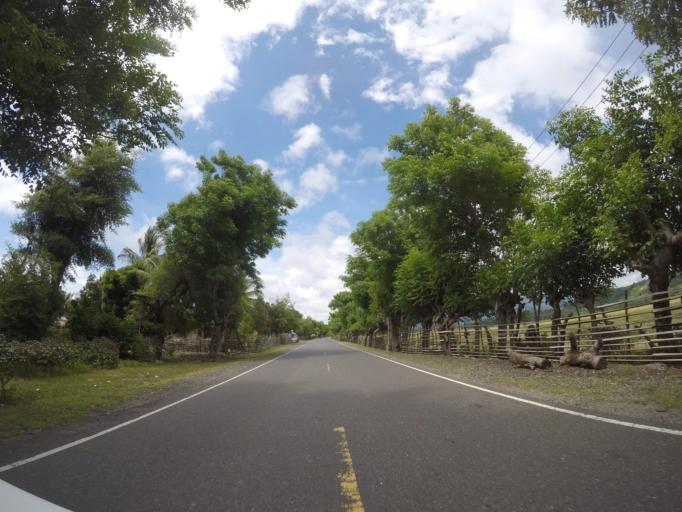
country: TL
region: Liquica
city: Maubara
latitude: -8.7610
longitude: 125.1006
